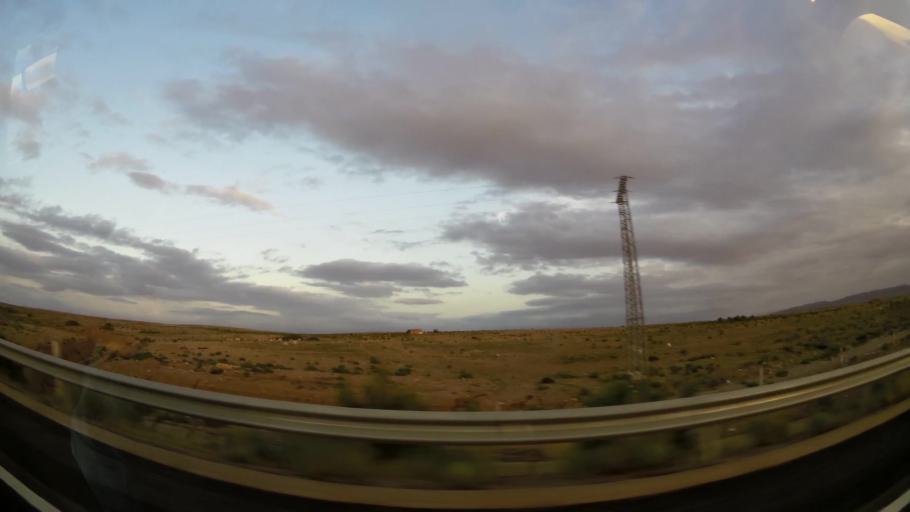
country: MA
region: Oriental
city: Taourirt
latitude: 34.5459
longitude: -2.9029
